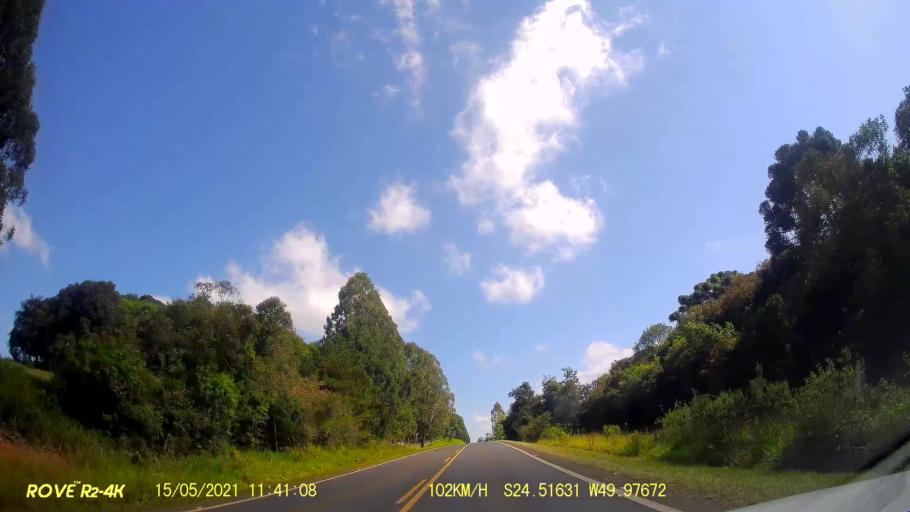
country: BR
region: Parana
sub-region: Pirai Do Sul
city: Pirai do Sul
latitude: -24.5163
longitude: -49.9767
